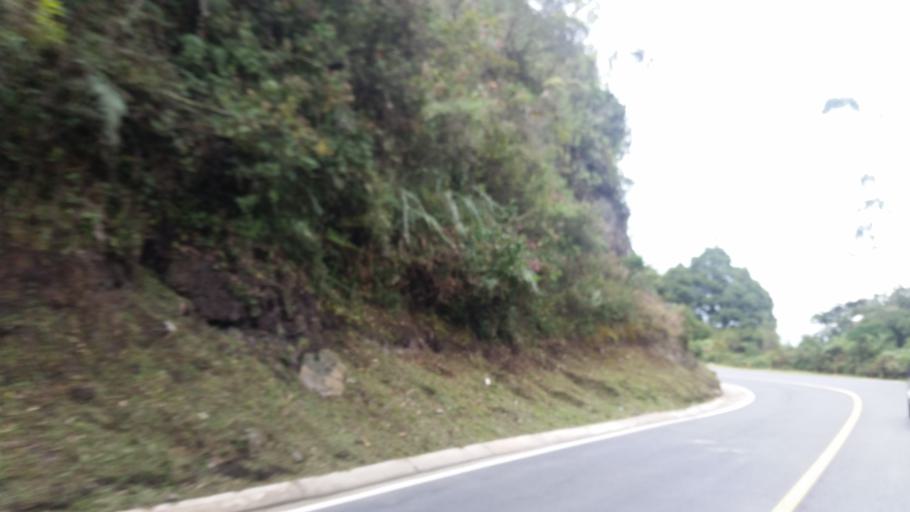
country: CO
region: Cundinamarca
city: Choachi
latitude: 4.5544
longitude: -73.9472
